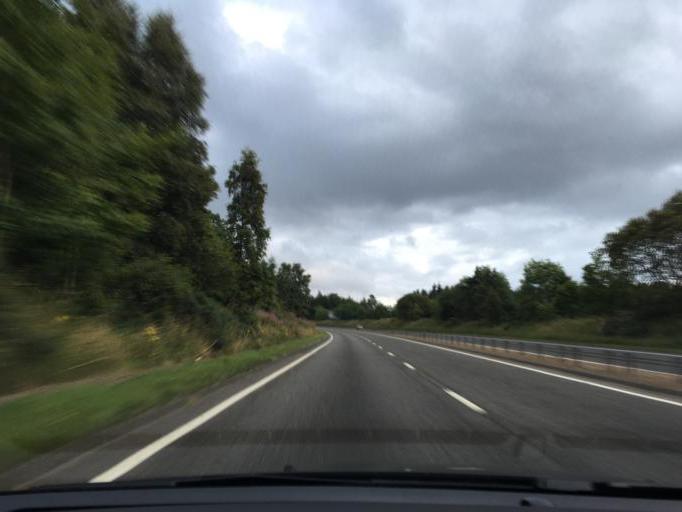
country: GB
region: Scotland
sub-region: Highland
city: Inverness
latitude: 57.4590
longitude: -4.1667
